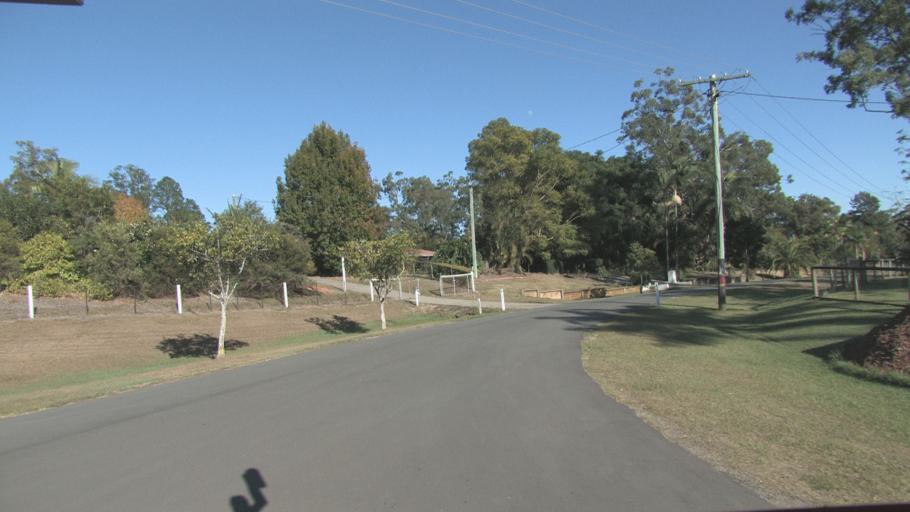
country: AU
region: Queensland
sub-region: Brisbane
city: Forest Lake
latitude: -27.6666
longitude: 153.0011
